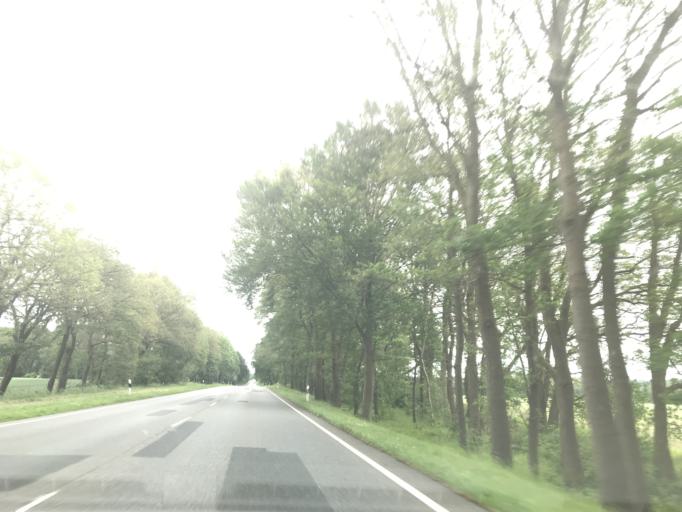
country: DE
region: Lower Saxony
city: Loxstedt
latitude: 53.4906
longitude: 8.6555
